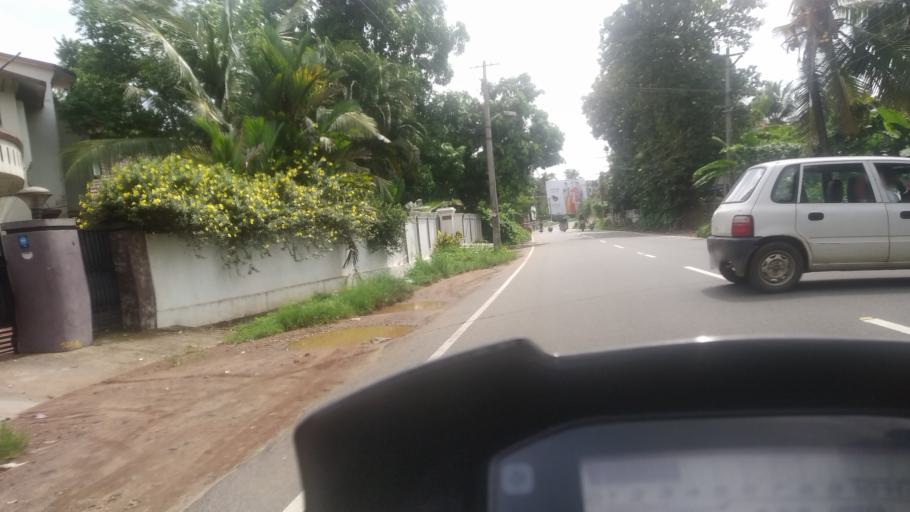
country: IN
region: Kerala
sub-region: Ernakulam
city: Aluva
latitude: 10.1291
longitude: 76.2957
